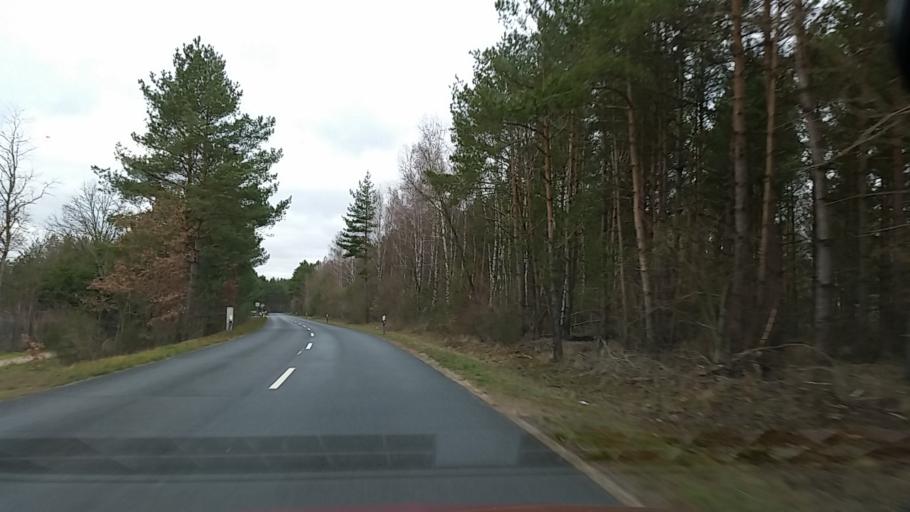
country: DE
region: Lower Saxony
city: Bodenteich
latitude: 52.8451
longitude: 10.6639
